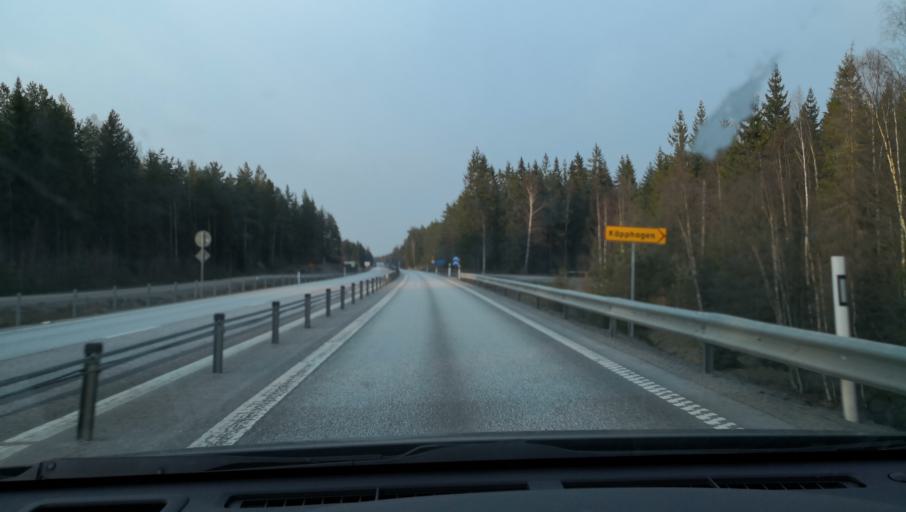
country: SE
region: OErebro
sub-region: Lindesbergs Kommun
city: Lindesberg
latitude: 59.5187
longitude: 15.1835
